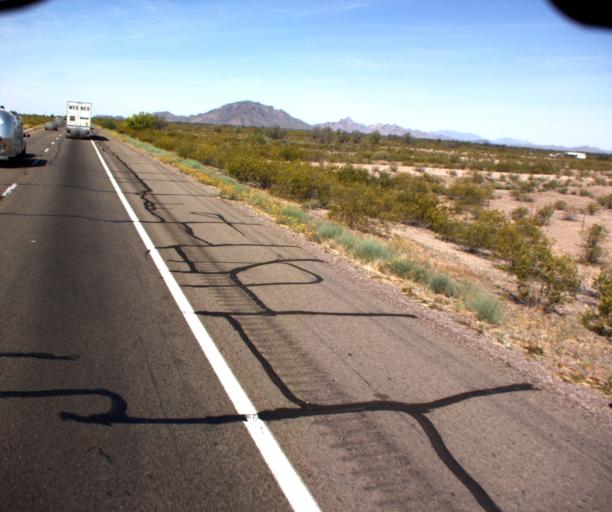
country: US
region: Arizona
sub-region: Maricopa County
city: Buckeye
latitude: 33.5046
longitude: -112.9735
